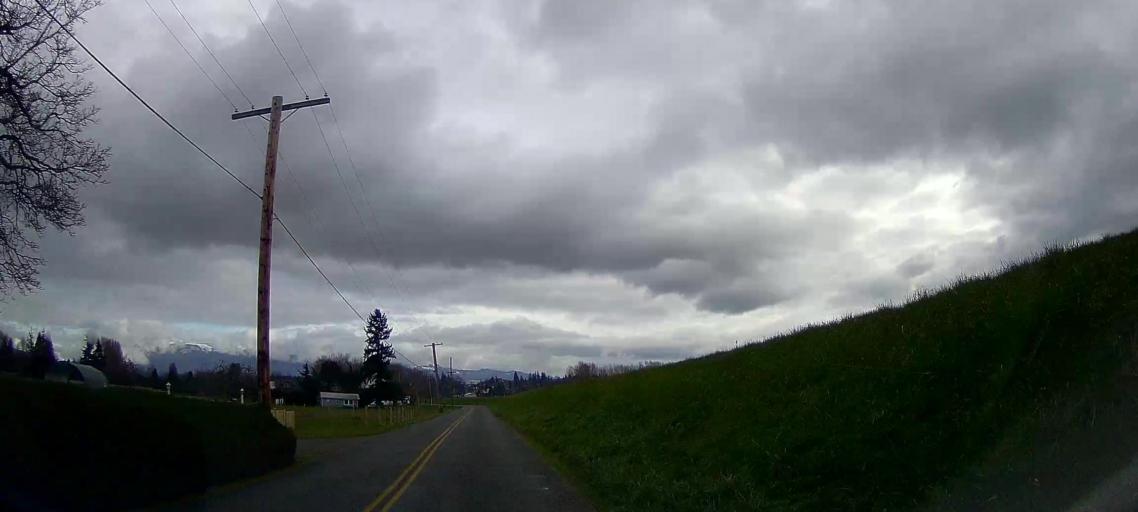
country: US
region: Washington
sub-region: Skagit County
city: Mount Vernon
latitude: 48.4307
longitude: -122.3542
